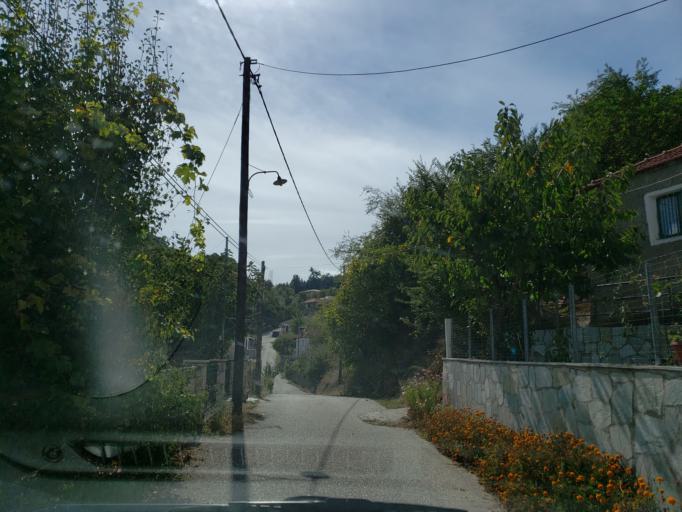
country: GR
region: Thessaly
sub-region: Trikala
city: Kastraki
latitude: 39.7756
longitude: 21.6603
